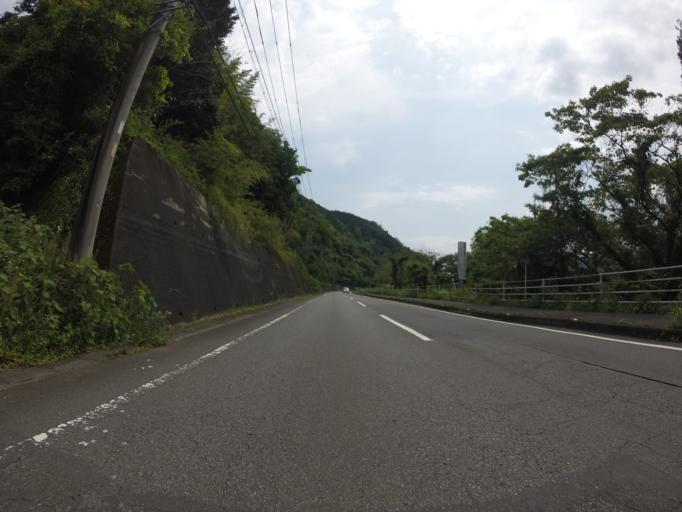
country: JP
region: Shizuoka
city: Shizuoka-shi
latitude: 35.0837
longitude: 138.3762
